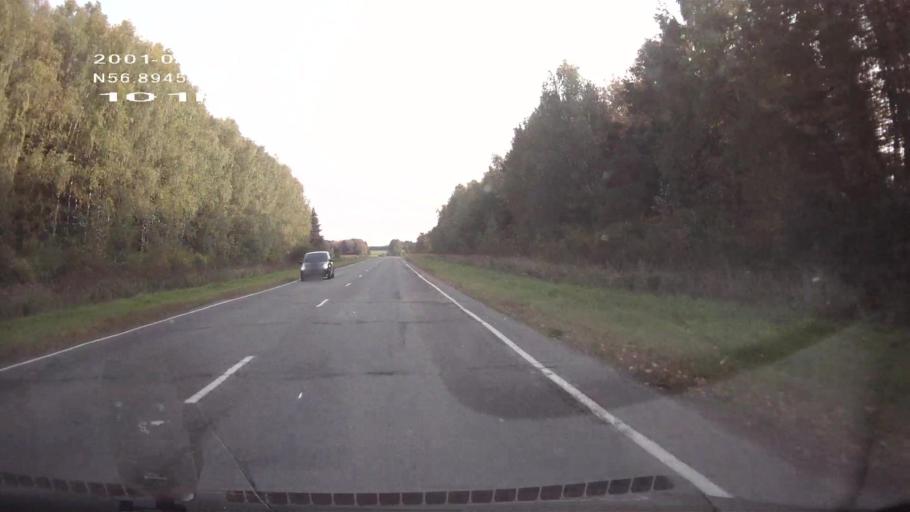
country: RU
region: Mariy-El
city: Kuzhener
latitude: 56.8930
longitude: 48.7520
